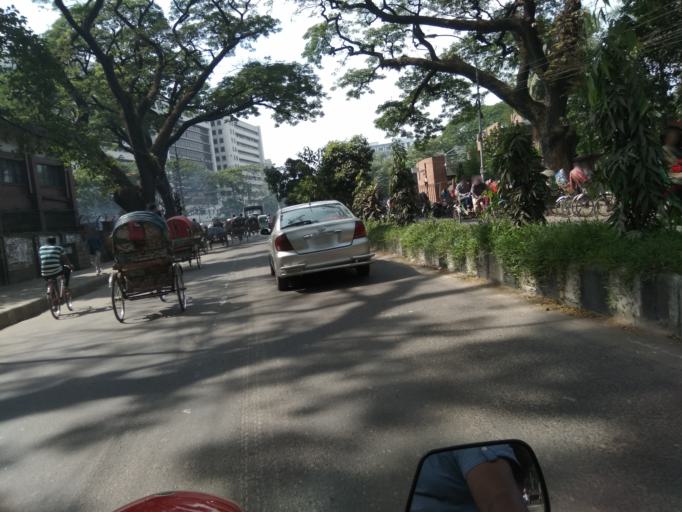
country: BD
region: Dhaka
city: Azimpur
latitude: 23.7277
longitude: 90.3903
